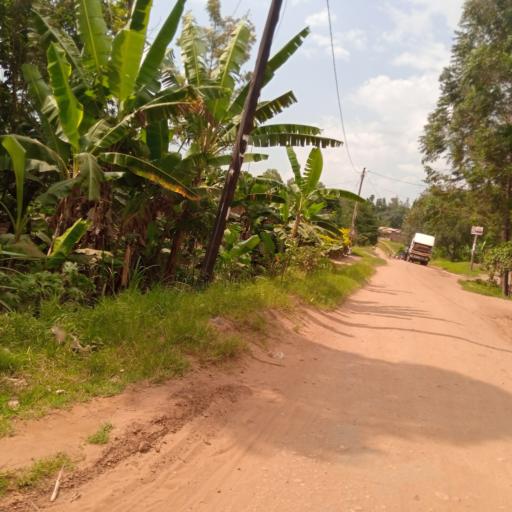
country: UG
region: Eastern Region
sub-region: Mbale District
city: Mbale
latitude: 1.1069
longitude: 34.2001
